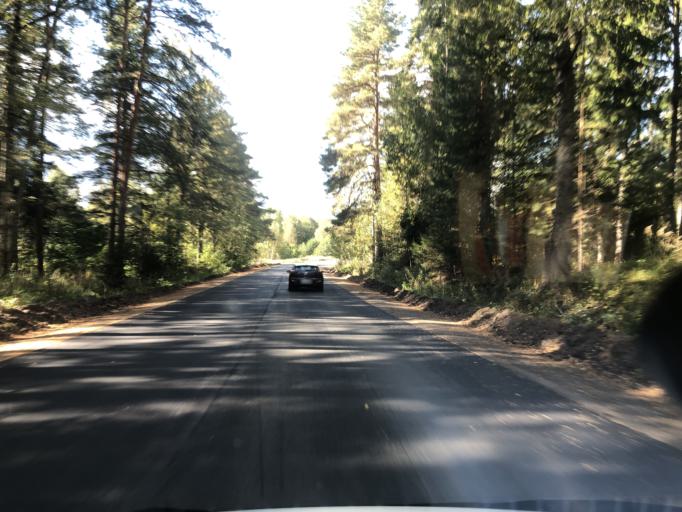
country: RU
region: Jaroslavl
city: Porech'ye-Rybnoye
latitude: 56.9714
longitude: 39.4190
